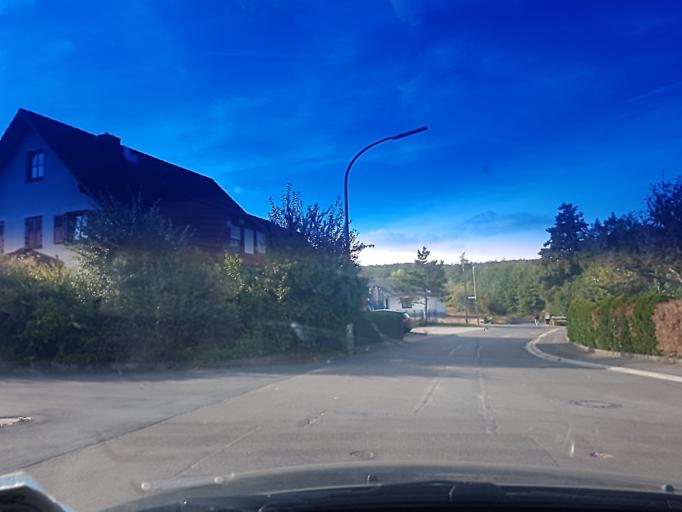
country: DE
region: Bavaria
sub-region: Regierungsbezirk Mittelfranken
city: Burghaslach
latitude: 49.7770
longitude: 10.5561
